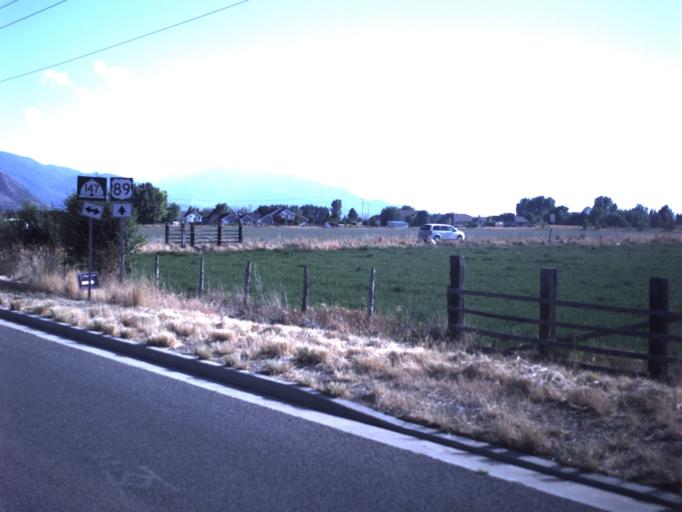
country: US
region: Utah
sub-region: Utah County
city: Mapleton
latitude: 40.1162
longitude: -111.5978
